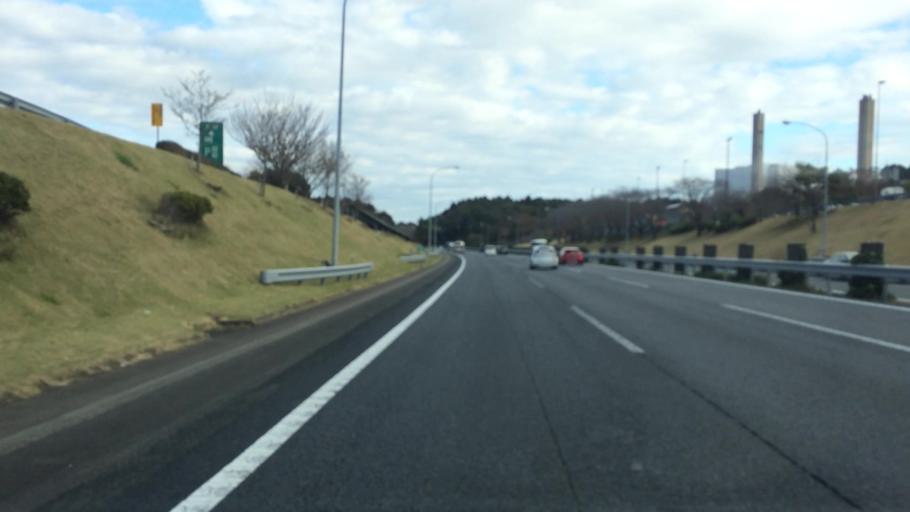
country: JP
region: Chiba
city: Shisui
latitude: 35.7099
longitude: 140.2837
